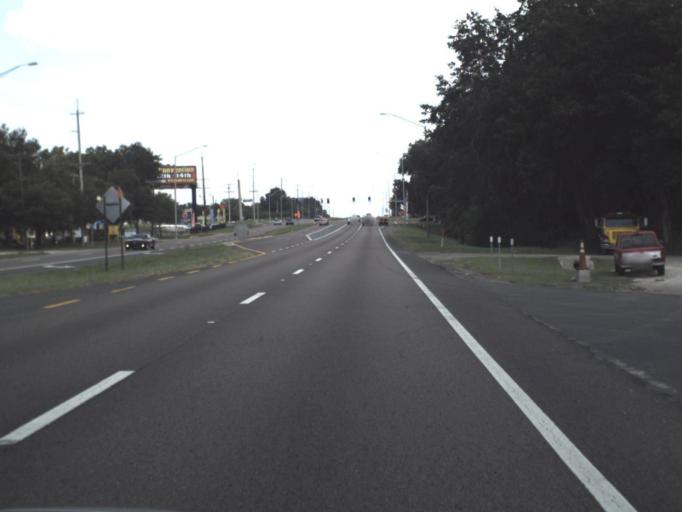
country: US
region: Florida
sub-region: Hillsborough County
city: Valrico
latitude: 27.9377
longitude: -82.2307
